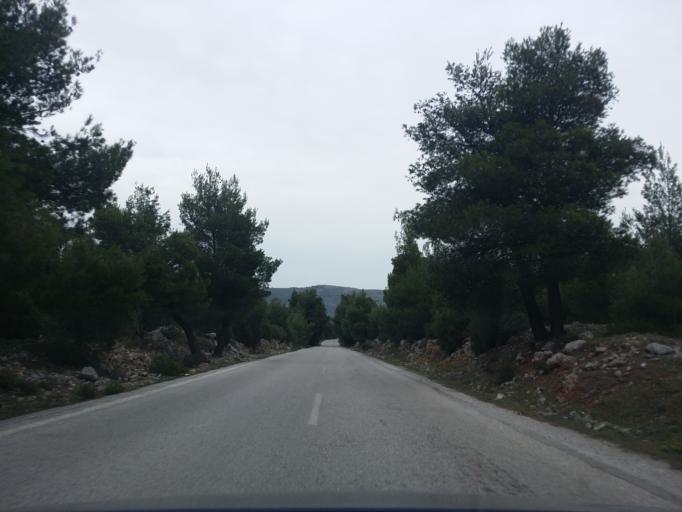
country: GR
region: Attica
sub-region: Nomarchia Dytikis Attikis
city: Vilia
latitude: 38.1484
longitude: 23.2967
